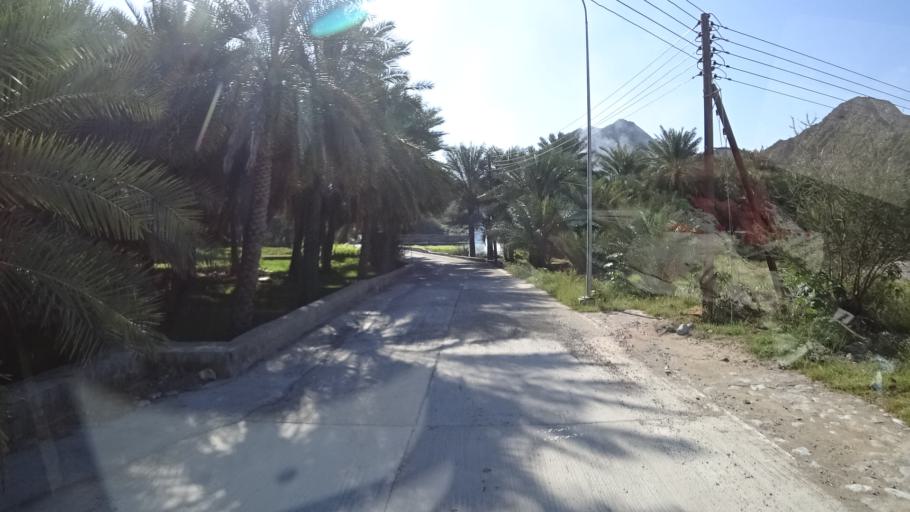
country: OM
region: Al Batinah
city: Bayt al `Awabi
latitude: 23.3783
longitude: 57.6633
